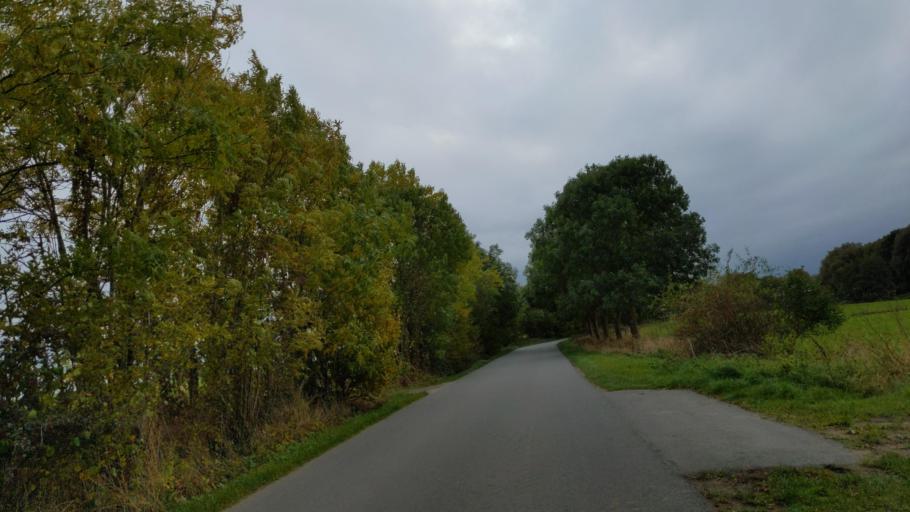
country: DE
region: Schleswig-Holstein
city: Sierksdorf
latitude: 54.0765
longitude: 10.7435
